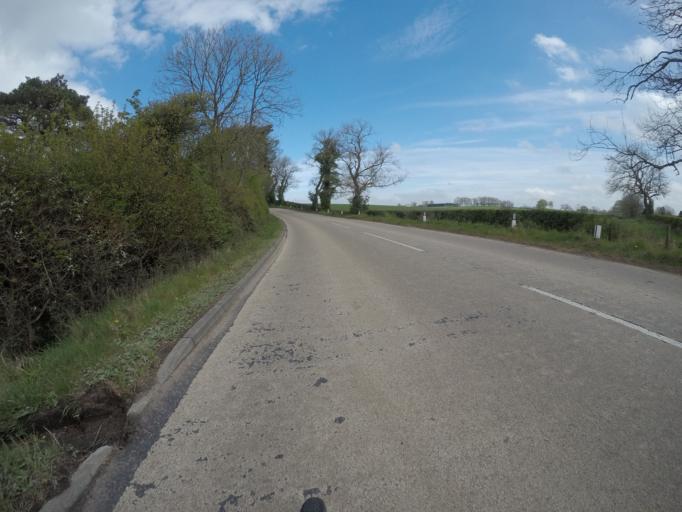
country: GB
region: Scotland
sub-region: East Ayrshire
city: Crosshouse
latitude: 55.6482
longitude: -4.5717
